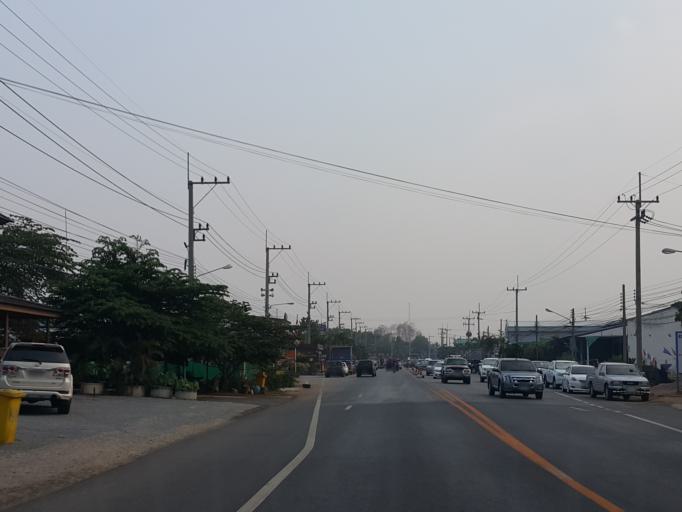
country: TH
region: Uthai Thani
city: Huai Khot
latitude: 15.1824
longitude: 99.6969
